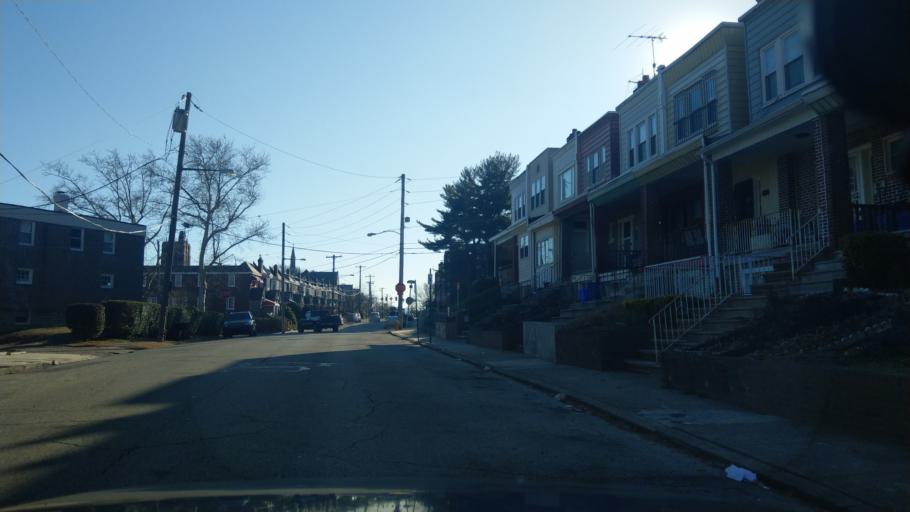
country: US
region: Pennsylvania
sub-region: Montgomery County
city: Wyndmoor
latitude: 40.0416
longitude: -75.1541
